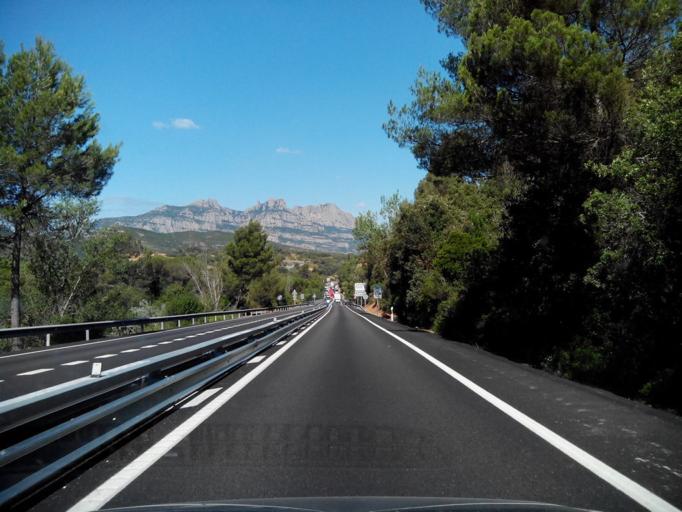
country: ES
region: Catalonia
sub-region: Provincia de Barcelona
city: Viladecavalls
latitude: 41.5852
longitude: 1.9262
